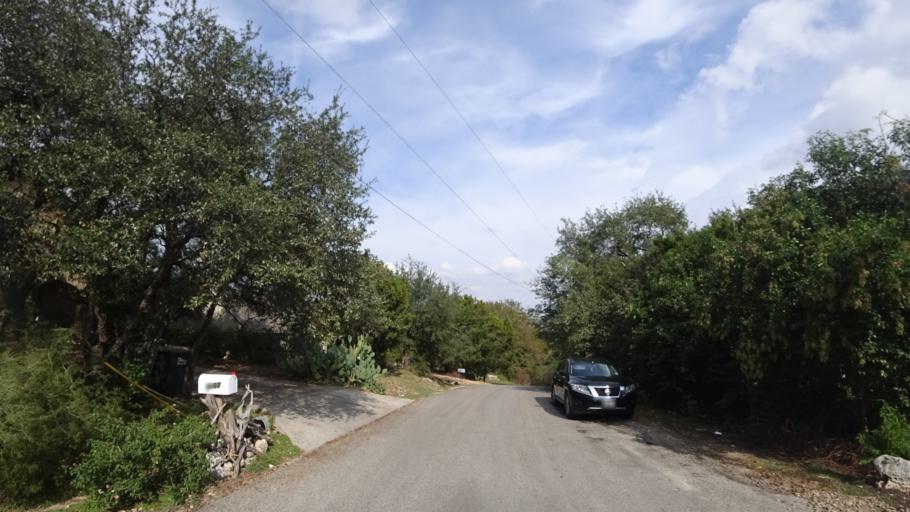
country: US
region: Texas
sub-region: Travis County
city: Hudson Bend
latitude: 30.3793
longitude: -97.9300
